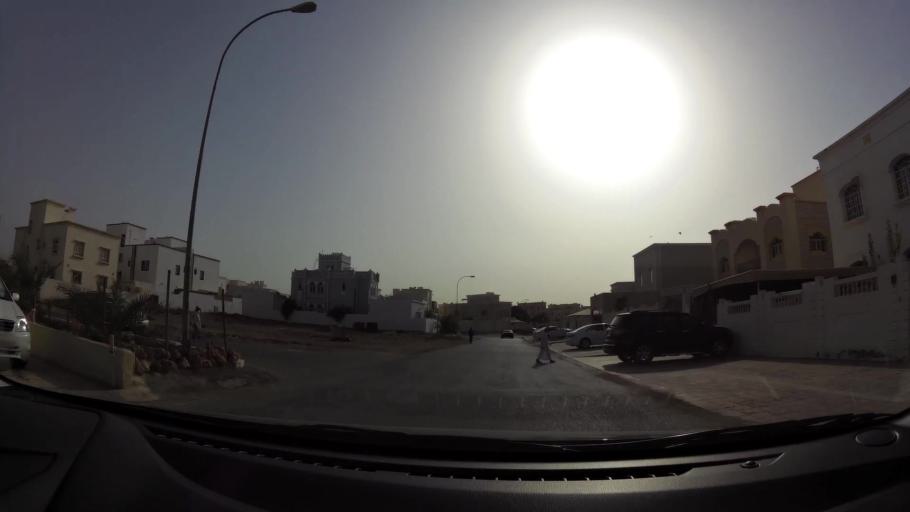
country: OM
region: Muhafazat Masqat
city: Bawshar
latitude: 23.5430
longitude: 58.3608
